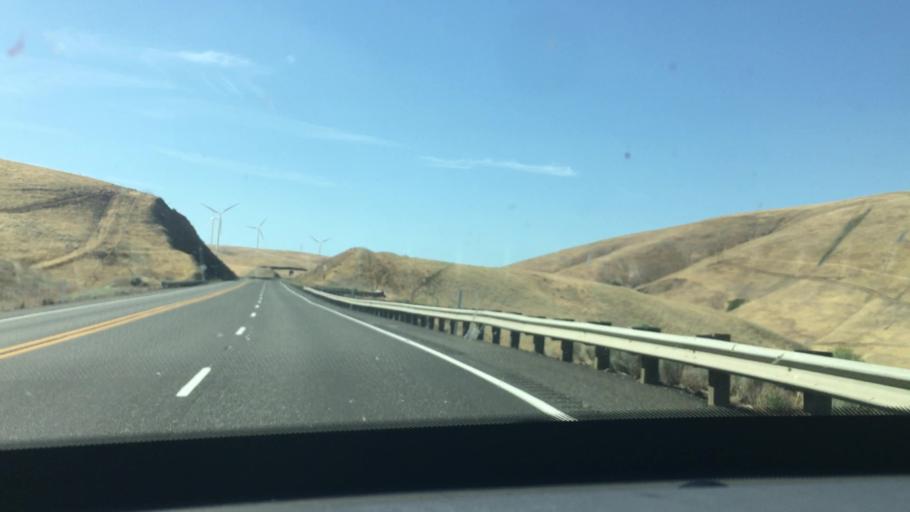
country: US
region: Washington
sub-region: Klickitat County
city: Goldendale
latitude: 45.7137
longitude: -120.8015
